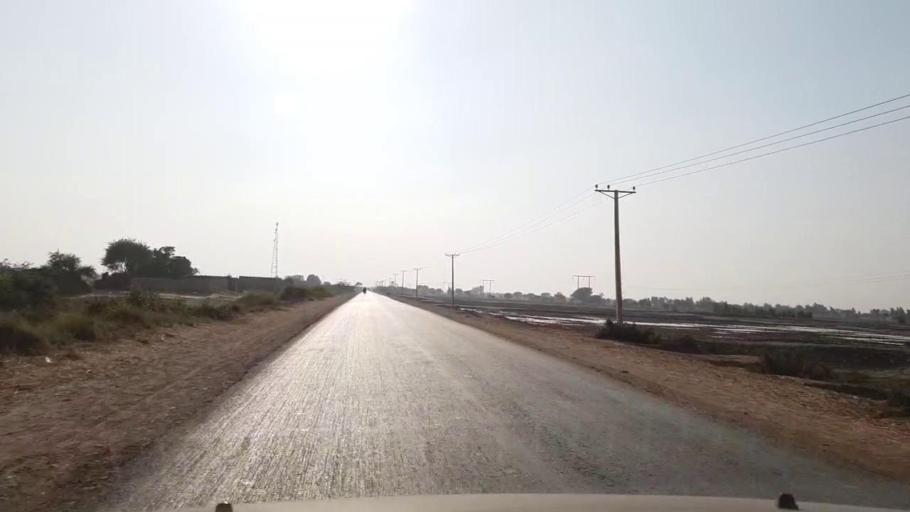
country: PK
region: Sindh
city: Bulri
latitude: 24.9985
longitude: 68.3883
